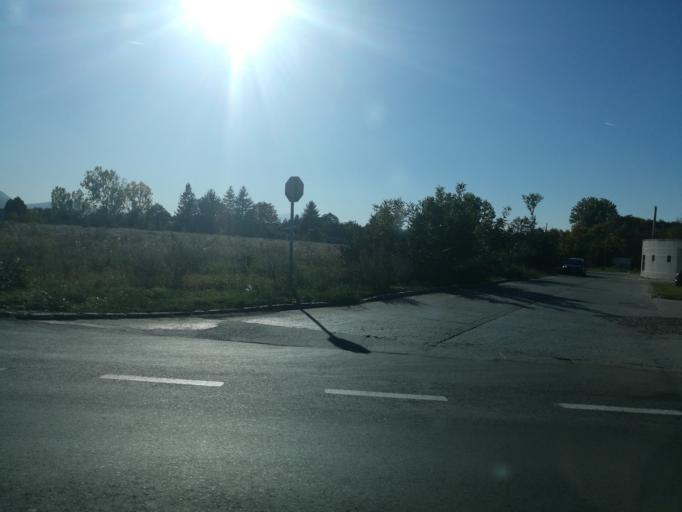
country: RO
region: Brasov
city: Brasov
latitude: 45.6788
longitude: 25.5868
